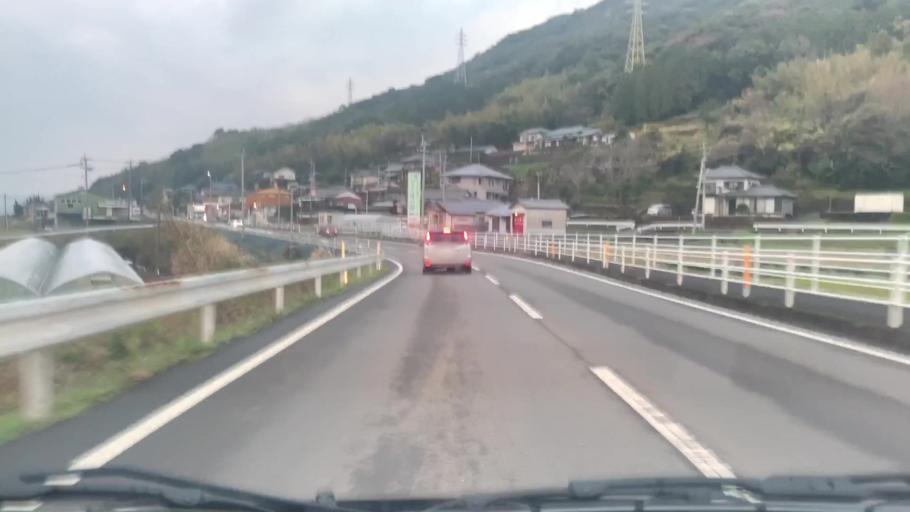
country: JP
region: Saga Prefecture
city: Ureshinomachi-shimojuku
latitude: 33.0526
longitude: 129.9293
